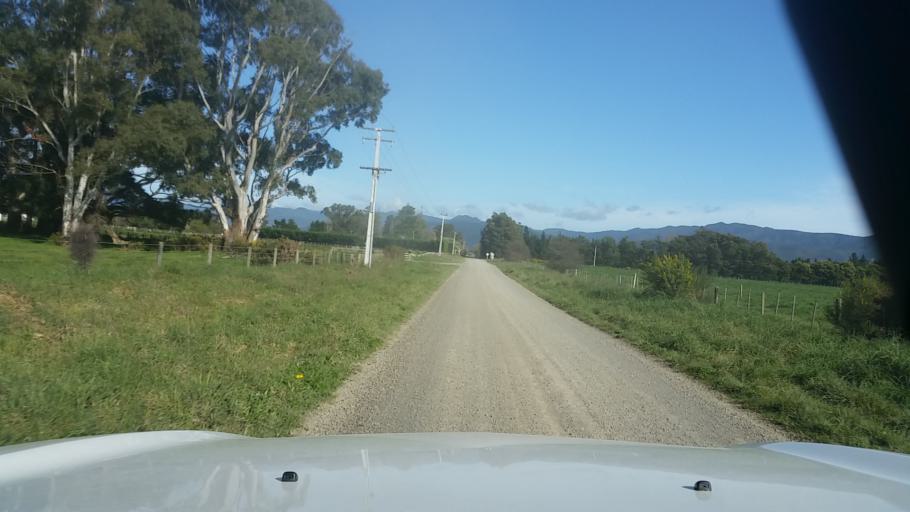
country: NZ
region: Wellington
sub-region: Masterton District
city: Masterton
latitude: -41.1187
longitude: 175.3920
